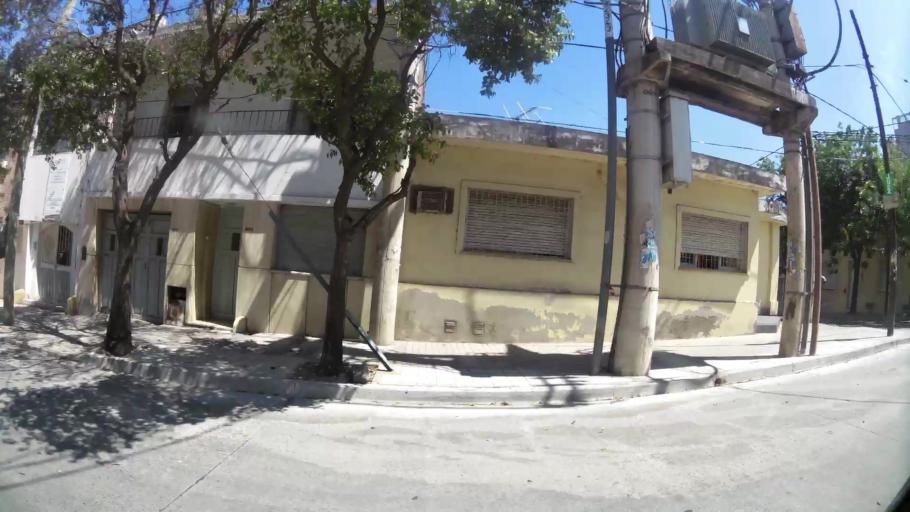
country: AR
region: Cordoba
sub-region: Departamento de Capital
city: Cordoba
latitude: -31.4039
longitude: -64.1932
